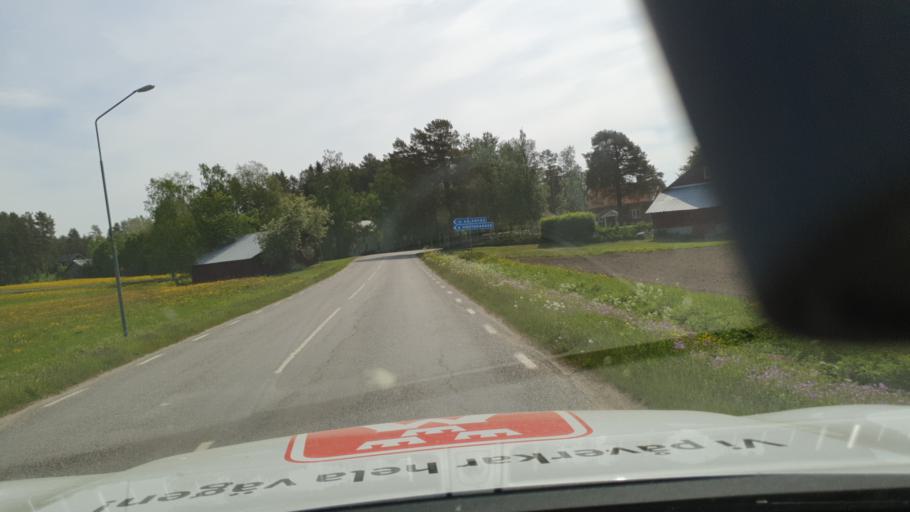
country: SE
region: Vaesterbotten
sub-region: Robertsfors Kommun
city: Robertsfors
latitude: 64.3010
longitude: 20.8761
